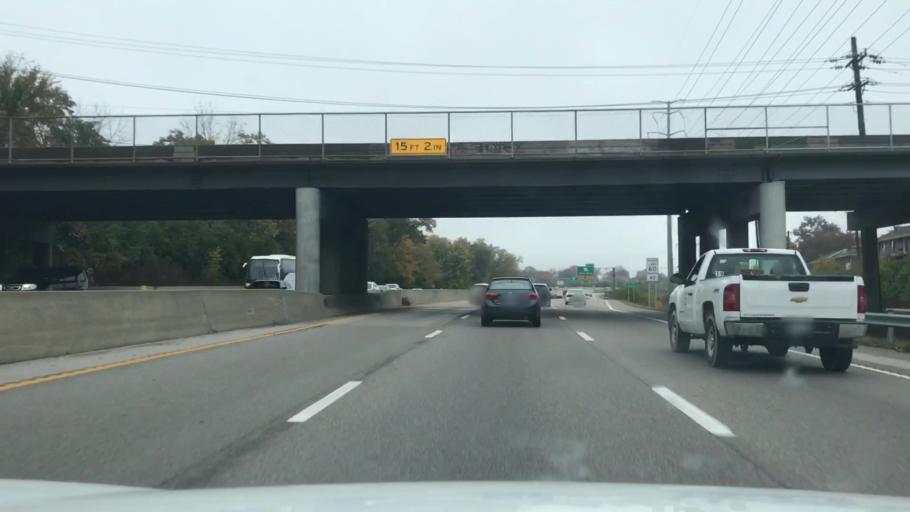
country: US
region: Missouri
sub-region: Saint Louis County
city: Olivette
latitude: 38.6677
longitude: -90.3611
